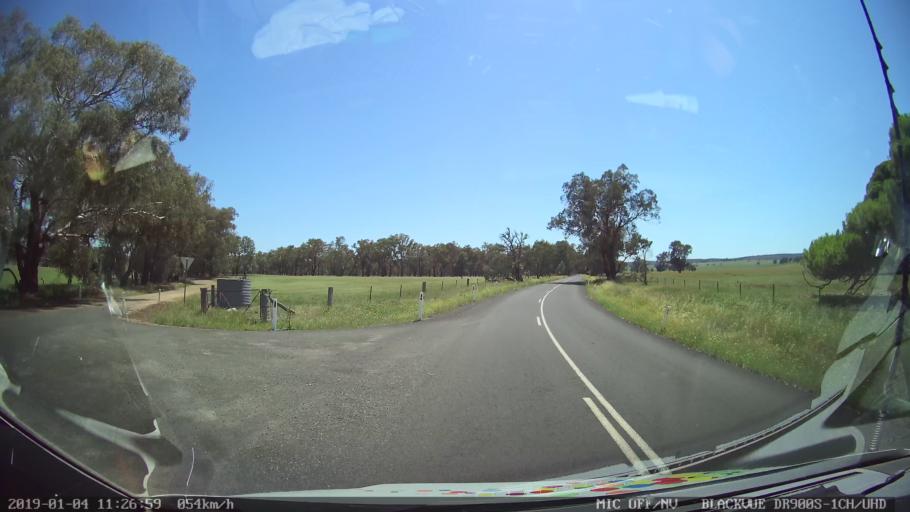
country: AU
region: New South Wales
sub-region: Cabonne
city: Molong
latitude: -33.1117
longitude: 148.7580
